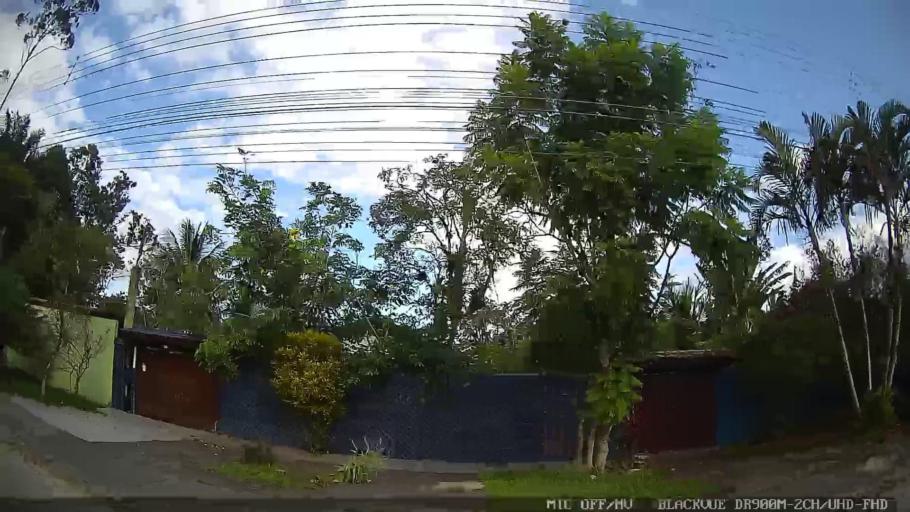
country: BR
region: Sao Paulo
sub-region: Caraguatatuba
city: Caraguatatuba
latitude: -23.6418
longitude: -45.4422
